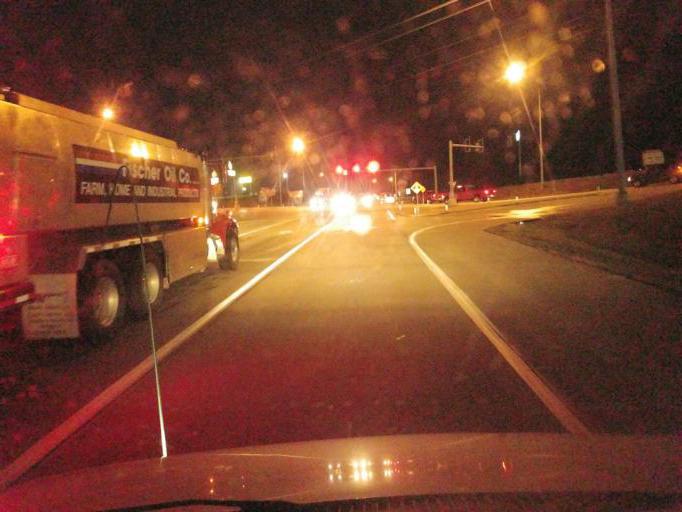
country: US
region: Missouri
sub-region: Franklin County
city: Villa Ridge
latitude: 38.4754
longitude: -90.8538
